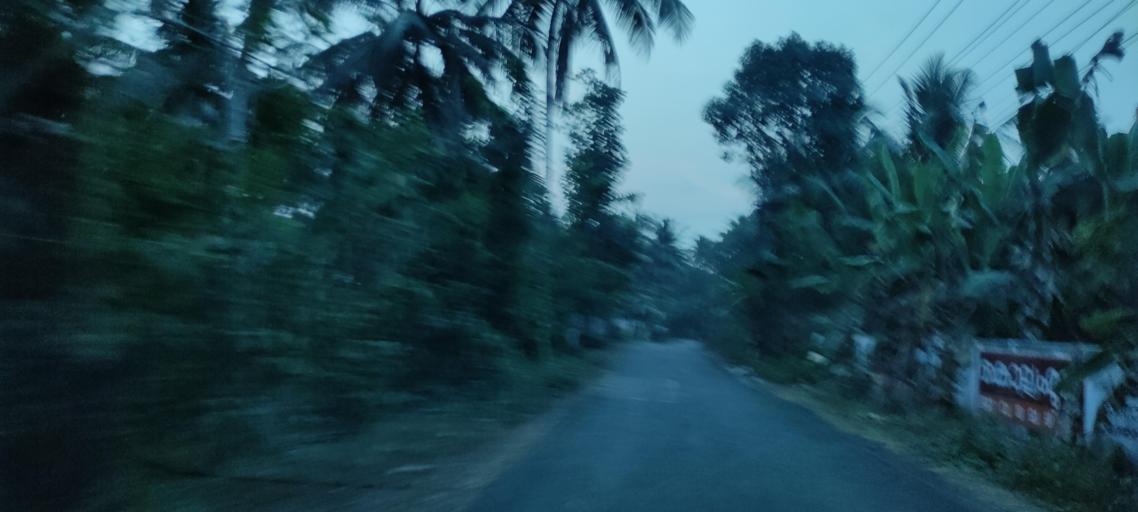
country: IN
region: Kerala
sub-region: Alappuzha
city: Mavelikara
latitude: 9.3308
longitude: 76.4859
